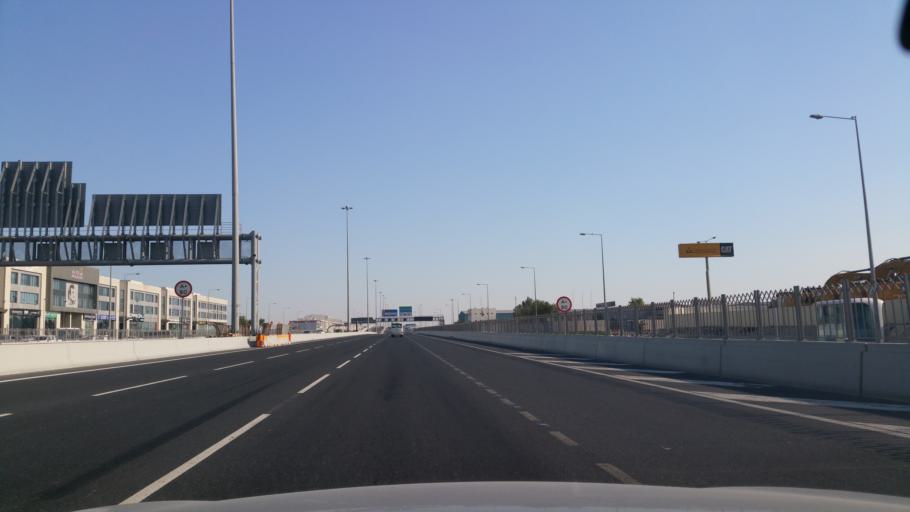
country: QA
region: Baladiyat ar Rayyan
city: Ar Rayyan
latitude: 25.2099
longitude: 51.4428
